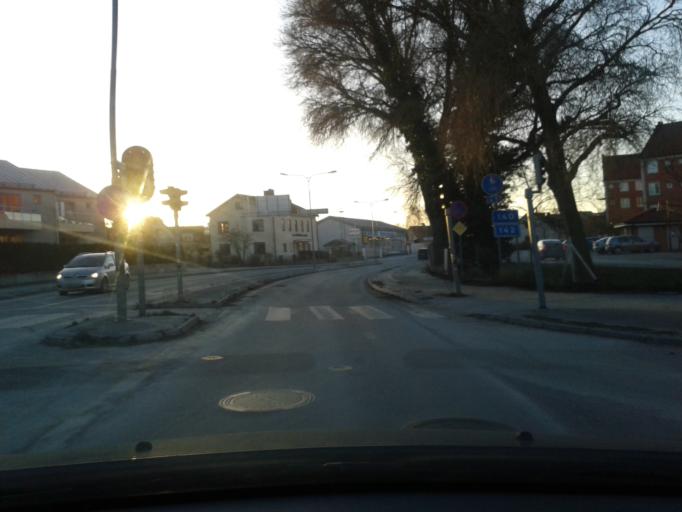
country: SE
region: Gotland
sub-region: Gotland
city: Visby
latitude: 57.6332
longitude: 18.2949
